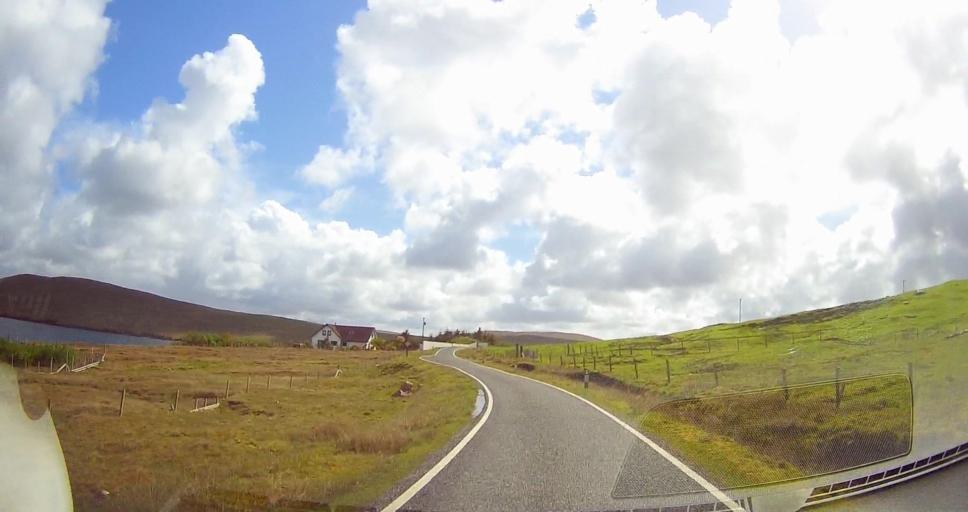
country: GB
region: Scotland
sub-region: Shetland Islands
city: Lerwick
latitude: 60.5375
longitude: -1.3566
